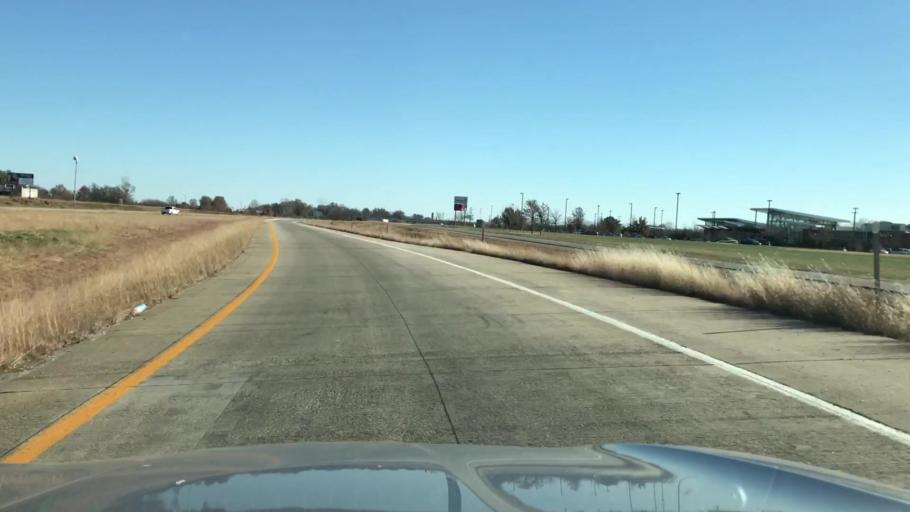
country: US
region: Missouri
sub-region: Jasper County
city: Carthage
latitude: 37.1386
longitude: -94.3223
